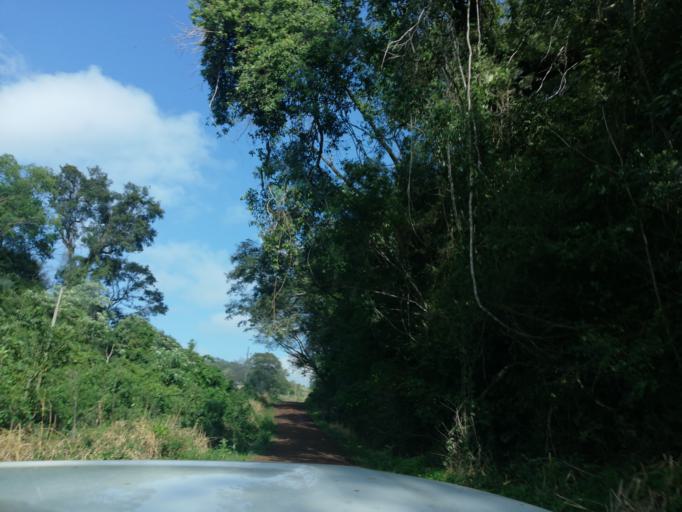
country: AR
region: Misiones
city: Cerro Azul
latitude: -27.6028
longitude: -55.5339
